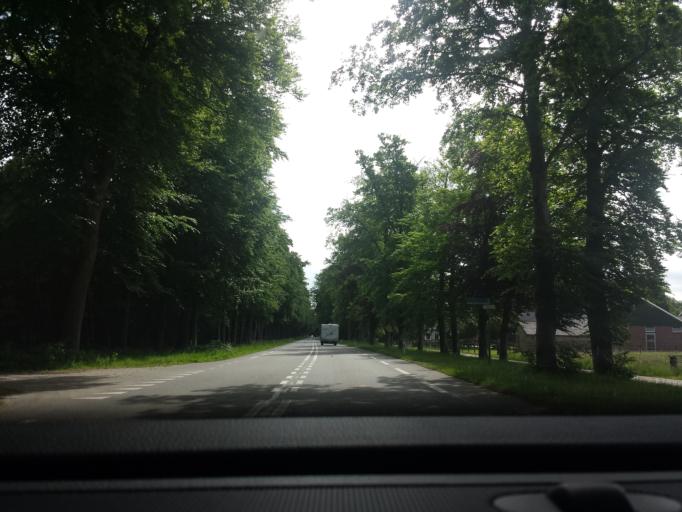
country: NL
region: Gelderland
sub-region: Gemeente Lochem
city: Lochem
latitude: 52.0992
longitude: 6.3709
